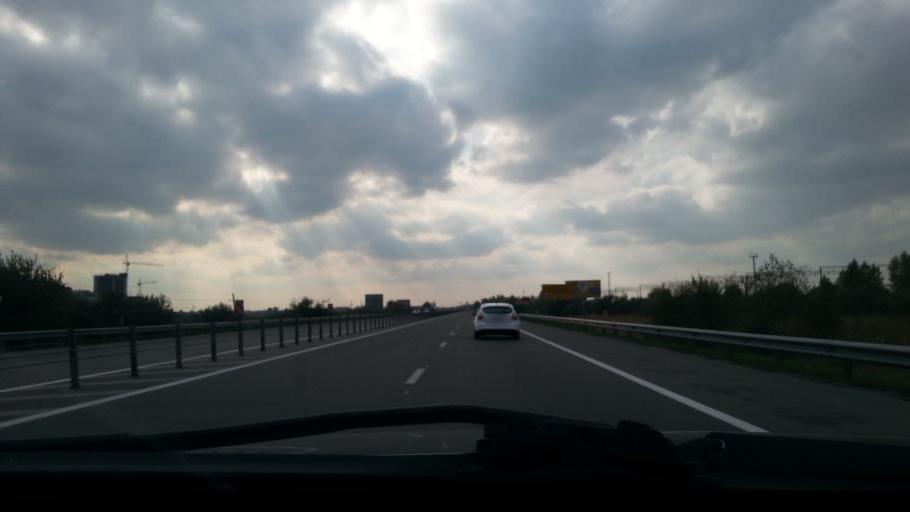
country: RU
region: Rostov
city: Bataysk
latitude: 47.1563
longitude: 39.7282
